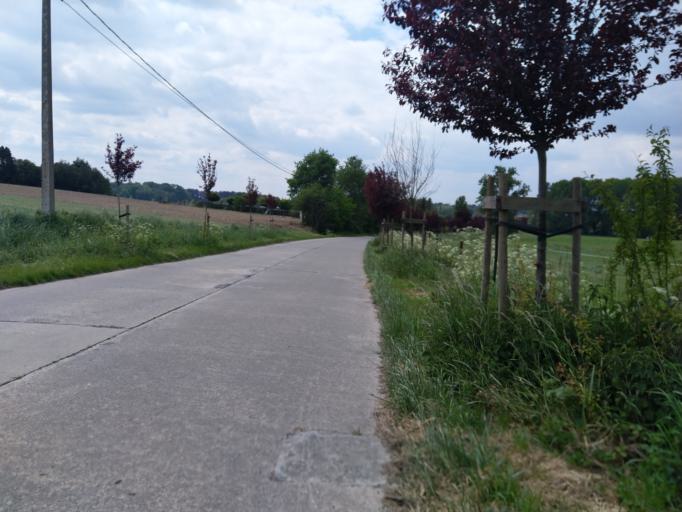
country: BE
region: Wallonia
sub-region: Province du Hainaut
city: Silly
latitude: 50.6061
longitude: 3.9517
